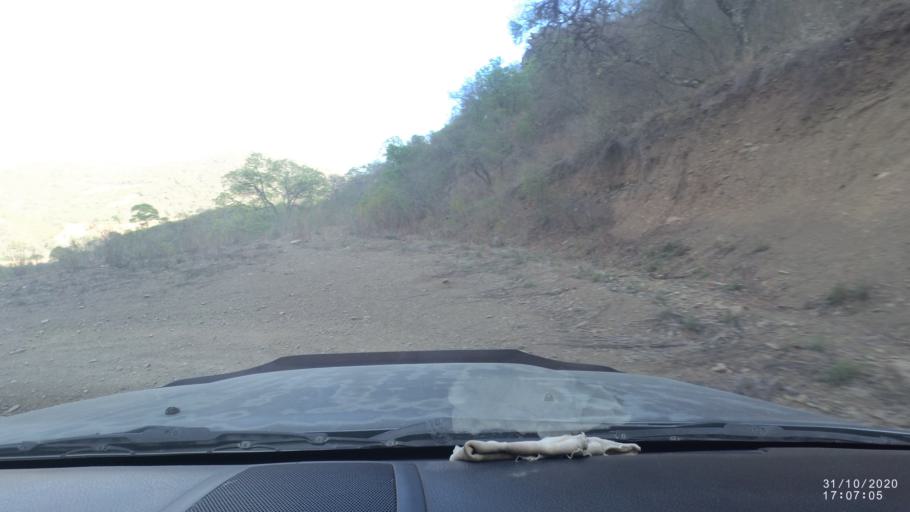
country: BO
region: Chuquisaca
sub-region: Provincia Zudanez
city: Mojocoya
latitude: -18.5455
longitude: -64.5433
